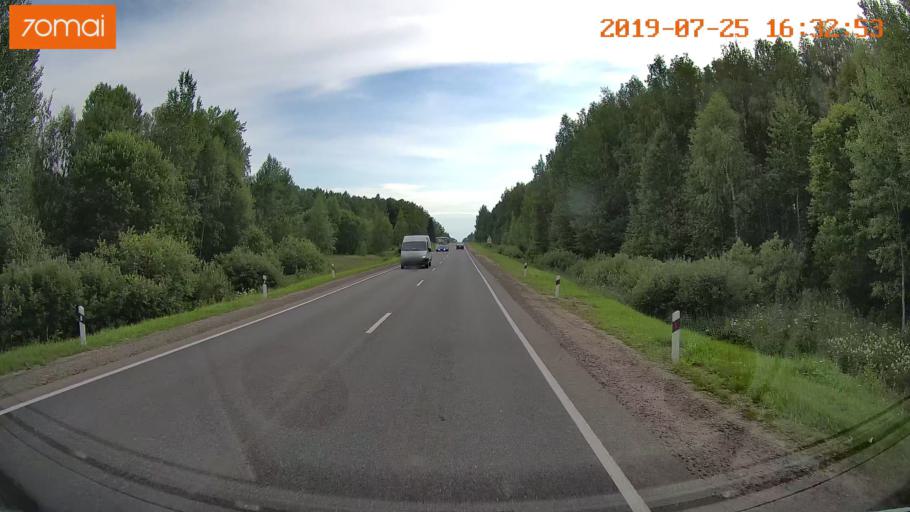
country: RU
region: Ivanovo
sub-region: Privolzhskiy Rayon
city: Ples
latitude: 57.4328
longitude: 41.4669
